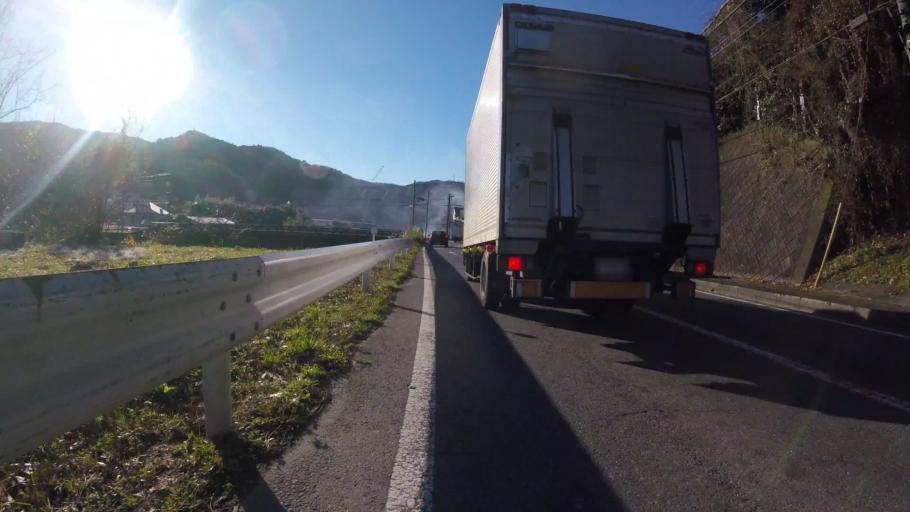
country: JP
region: Shizuoka
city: Heda
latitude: 34.9258
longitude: 138.9324
